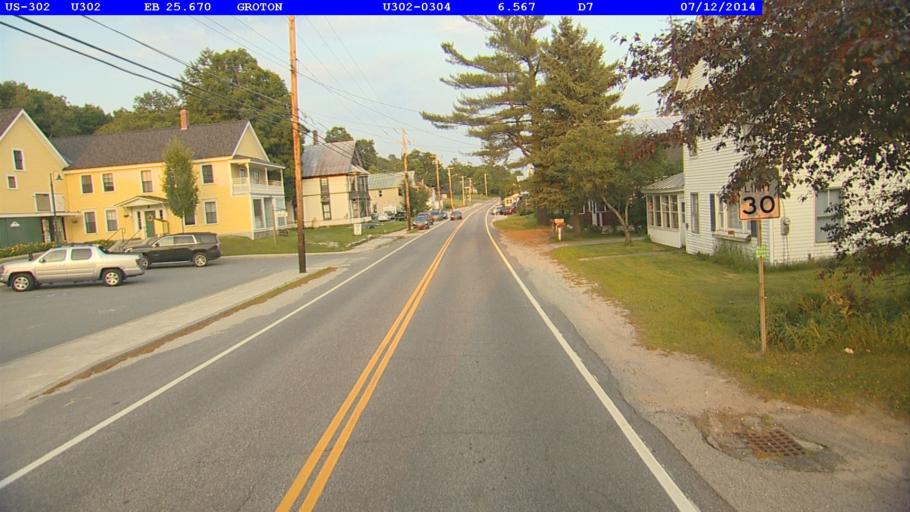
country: US
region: New Hampshire
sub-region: Grafton County
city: Woodsville
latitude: 44.2103
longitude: -72.1948
